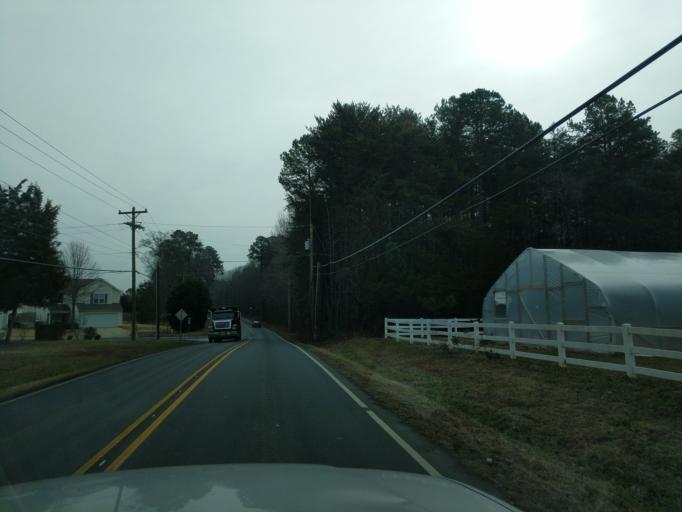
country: US
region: North Carolina
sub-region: Mecklenburg County
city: Charlotte
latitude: 35.3067
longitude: -80.8700
